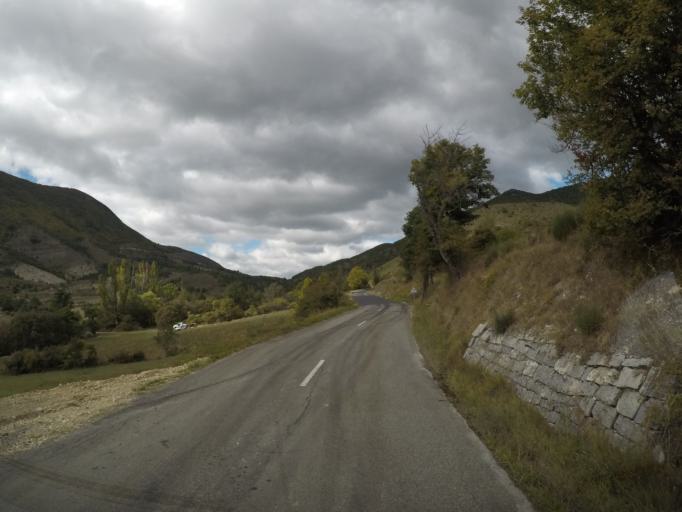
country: FR
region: Provence-Alpes-Cote d'Azur
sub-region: Departement du Vaucluse
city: Sault
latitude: 44.1763
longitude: 5.5877
